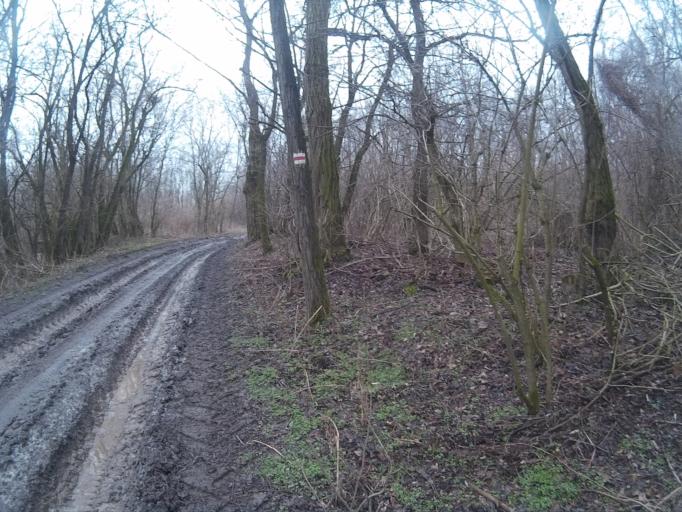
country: HU
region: Komarom-Esztergom
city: Tarjan
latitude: 47.5609
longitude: 18.5527
